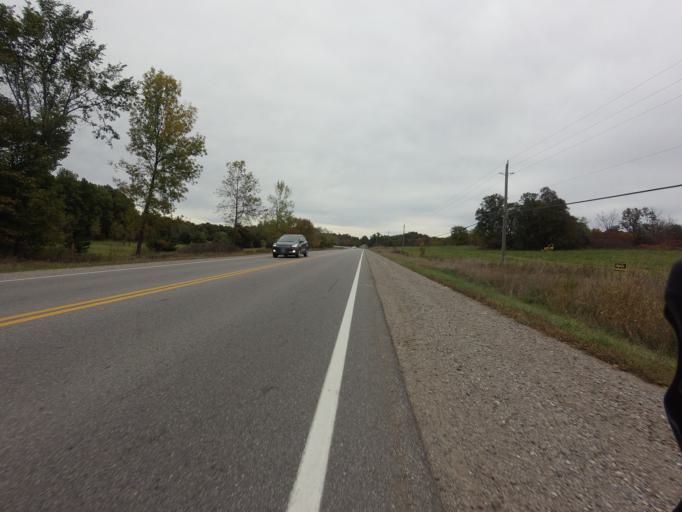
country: CA
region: Ontario
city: Gananoque
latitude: 44.4814
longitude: -76.2035
